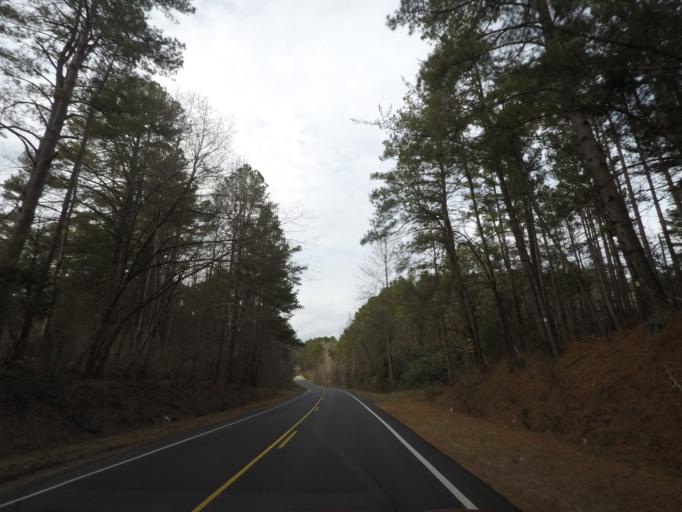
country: US
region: North Carolina
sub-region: Durham County
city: Durham
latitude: 36.0573
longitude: -78.9759
